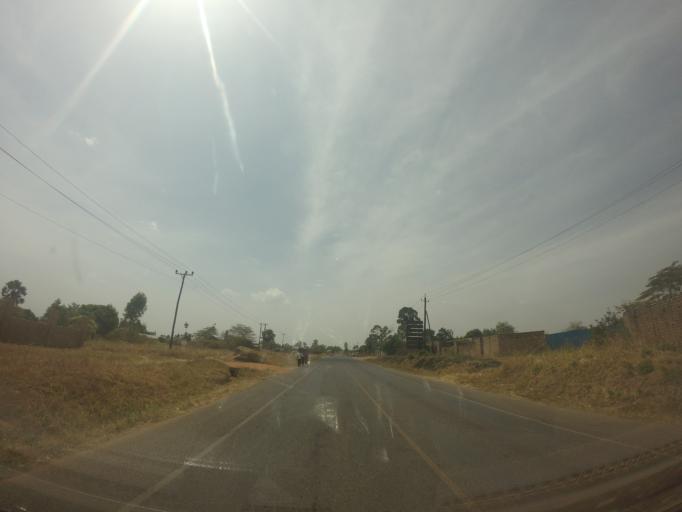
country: UG
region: Northern Region
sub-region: Arua District
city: Arua
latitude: 2.9671
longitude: 30.9181
